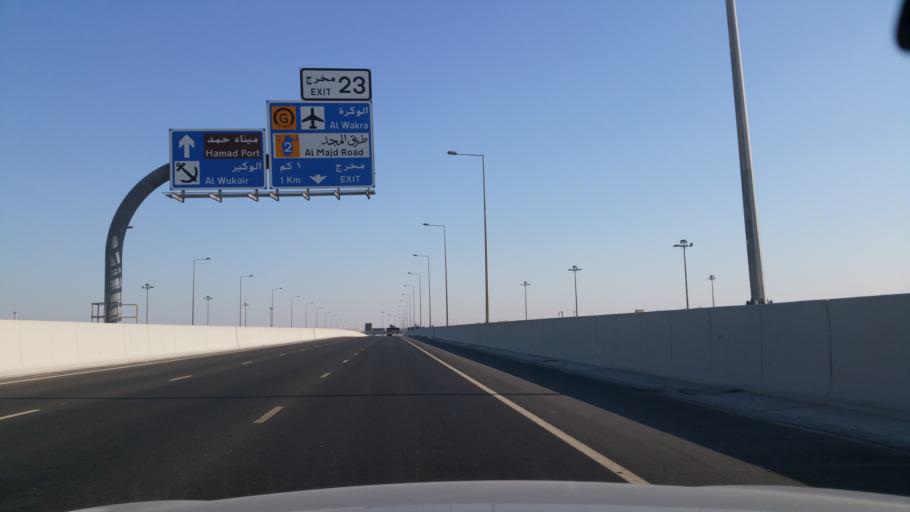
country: QA
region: Al Wakrah
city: Al Wukayr
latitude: 25.1804
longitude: 51.4643
